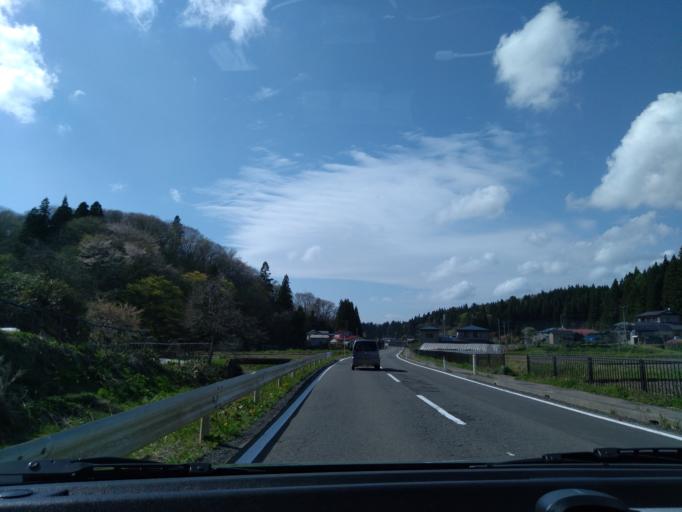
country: JP
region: Akita
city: Akita
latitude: 39.7086
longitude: 140.2060
